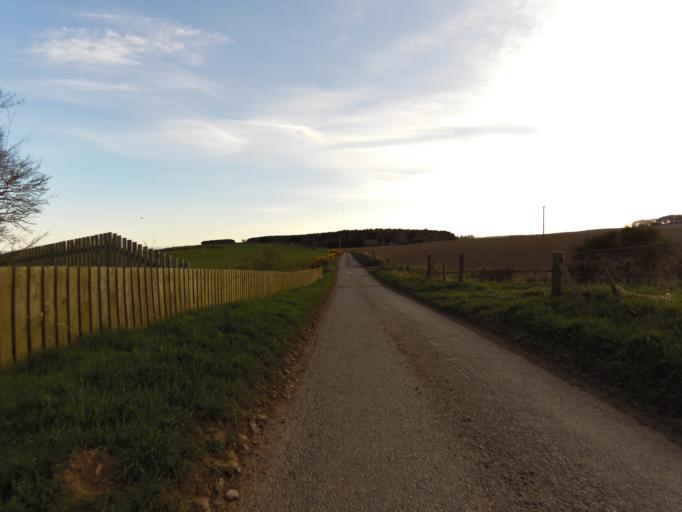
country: GB
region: Scotland
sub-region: Aberdeenshire
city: Stonehaven
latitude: 56.9313
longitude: -2.2265
